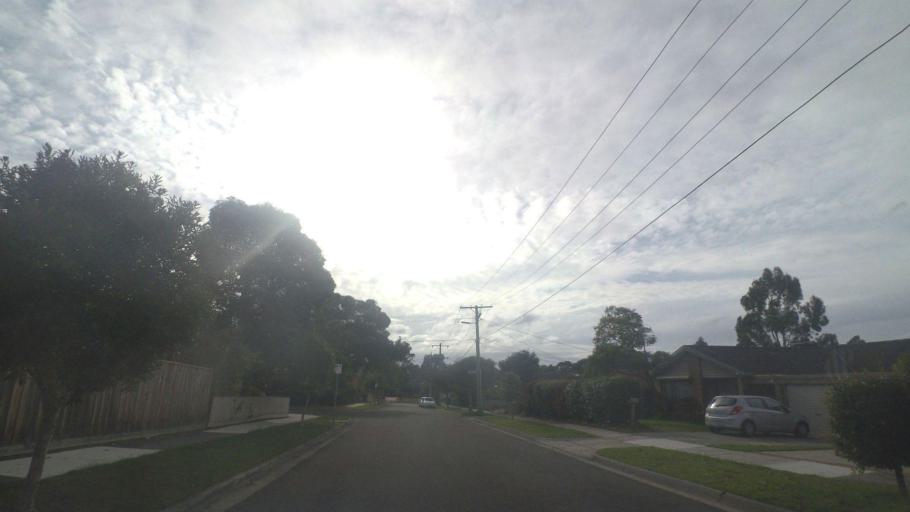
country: AU
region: Victoria
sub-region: Whitehorse
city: Vermont South
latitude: -37.8661
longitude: 145.1866
